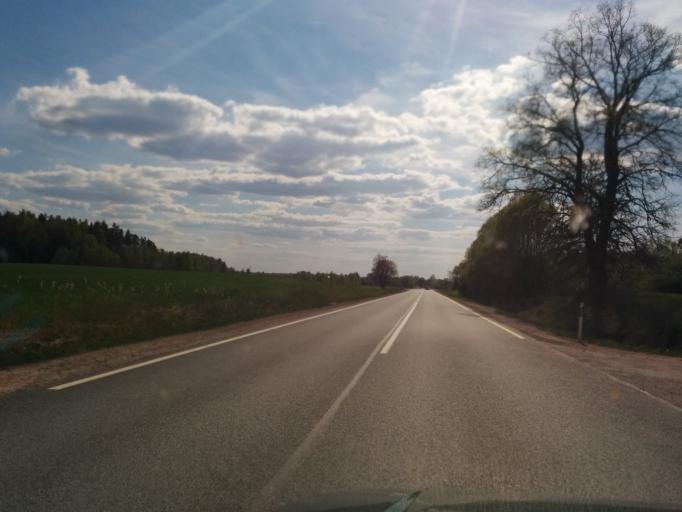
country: LV
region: Krimulda
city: Ragana
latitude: 57.1952
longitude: 24.7391
